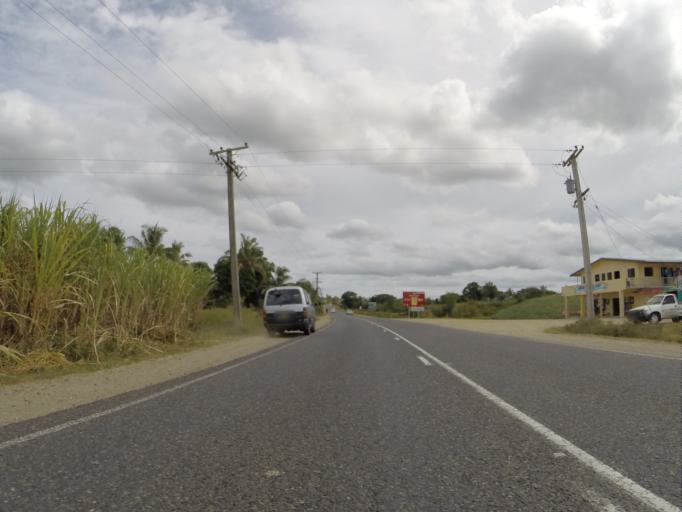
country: FJ
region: Western
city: Nadi
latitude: -18.0612
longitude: 177.3652
